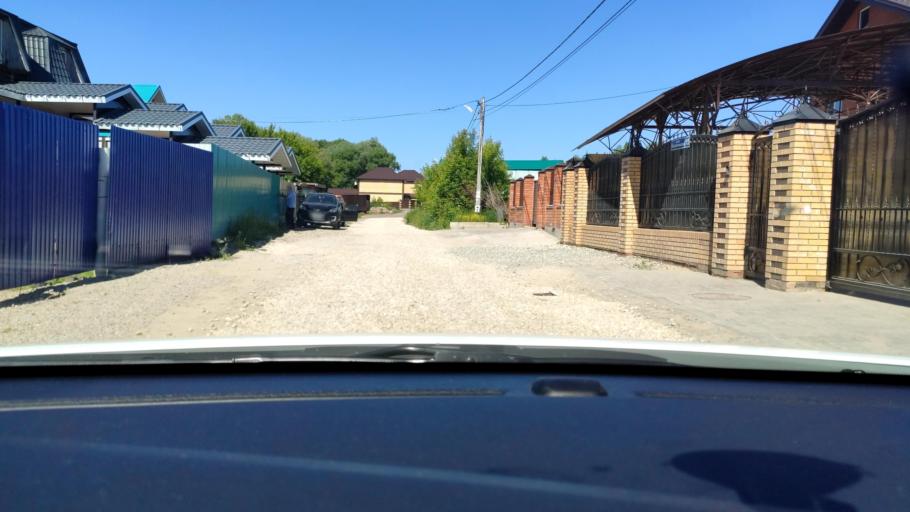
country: RU
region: Tatarstan
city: Stolbishchi
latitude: 55.7480
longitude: 49.2830
